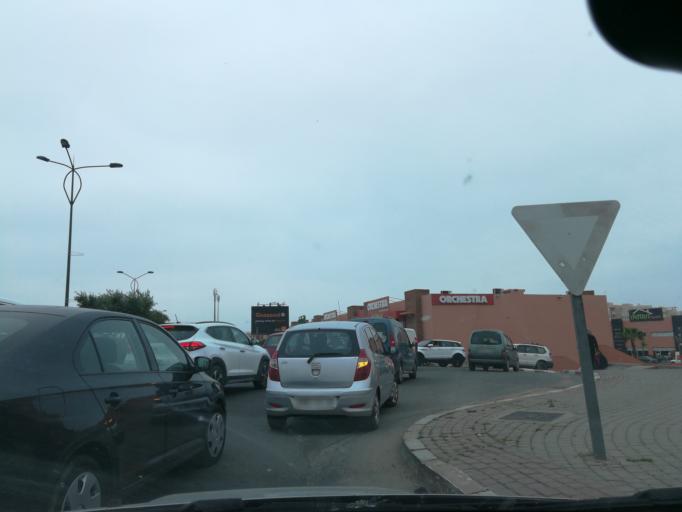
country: MA
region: Marrakech-Tensift-Al Haouz
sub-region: Marrakech
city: Marrakesh
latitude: 31.6686
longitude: -8.0119
